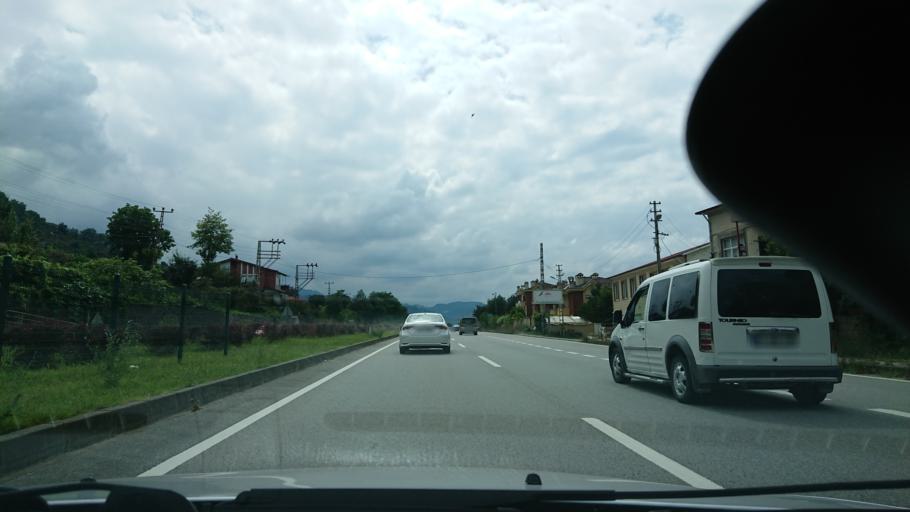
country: TR
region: Giresun
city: Kesap
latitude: 40.9282
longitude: 38.5579
